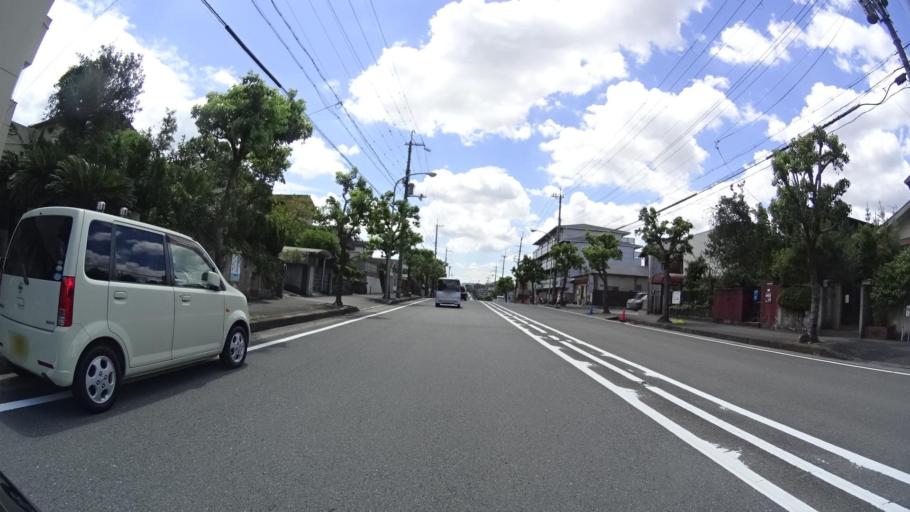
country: JP
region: Kyoto
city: Yawata
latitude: 34.8629
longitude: 135.6939
